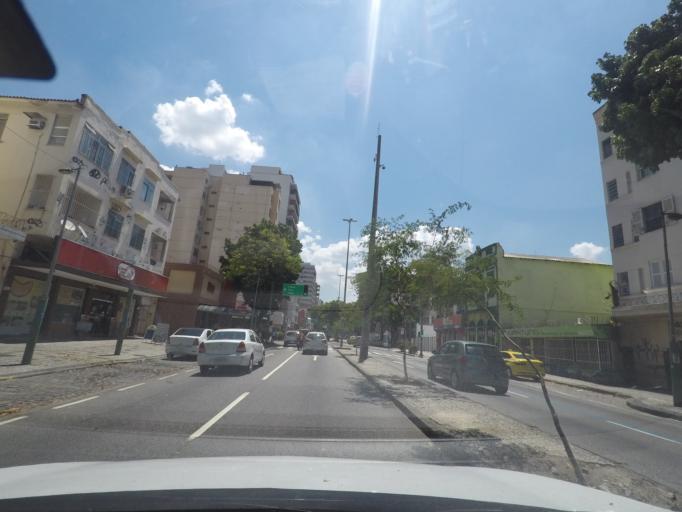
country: BR
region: Rio de Janeiro
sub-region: Rio De Janeiro
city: Rio de Janeiro
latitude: -22.9148
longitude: -43.2402
